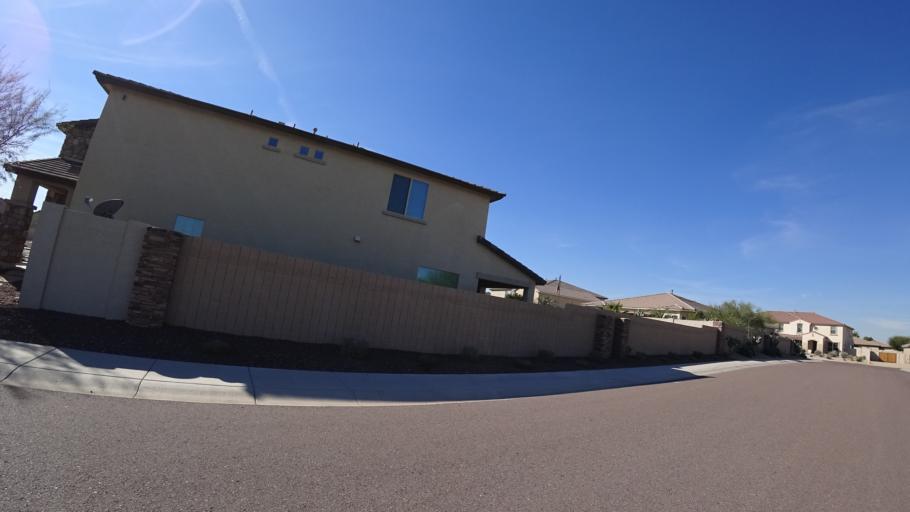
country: US
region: Arizona
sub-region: Maricopa County
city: Citrus Park
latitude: 33.5135
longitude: -112.4571
